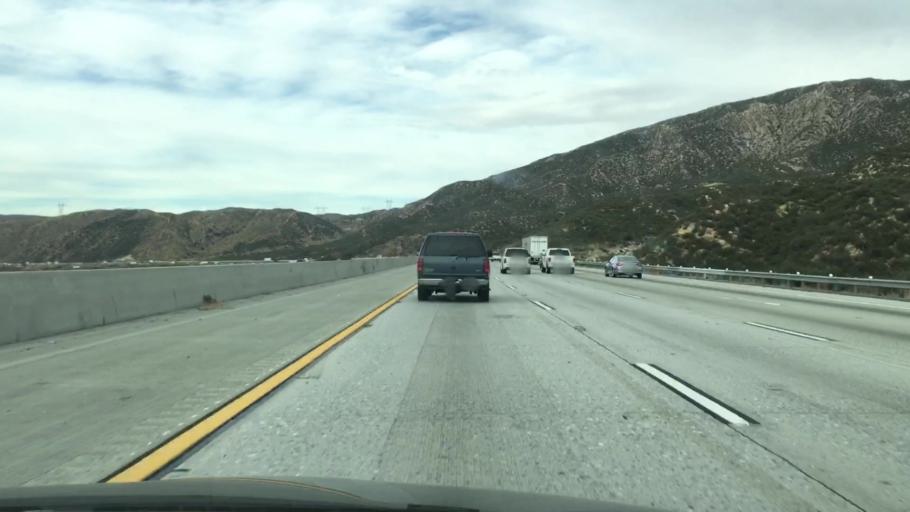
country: US
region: California
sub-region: San Bernardino County
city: Oak Hills
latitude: 34.2837
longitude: -117.4519
